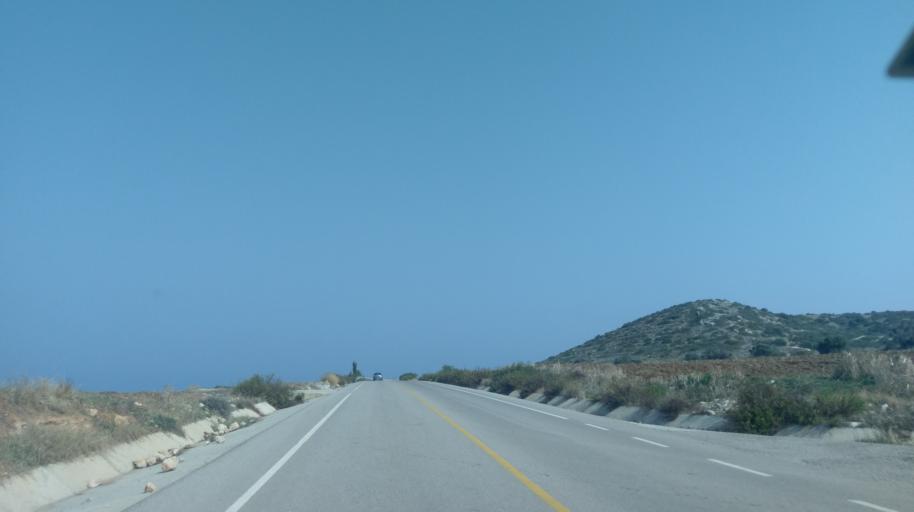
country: CY
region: Ammochostos
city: Leonarisso
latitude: 35.4890
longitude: 34.0793
